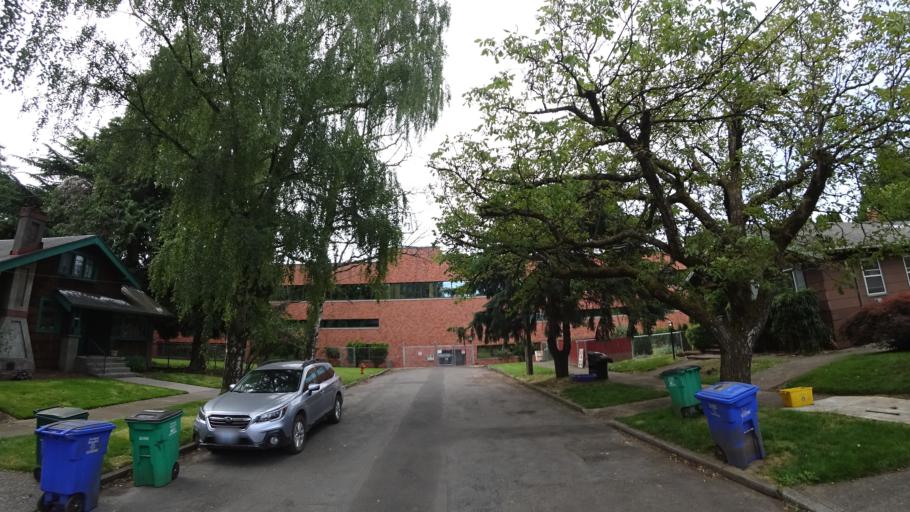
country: US
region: Oregon
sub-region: Multnomah County
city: Portland
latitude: 45.5328
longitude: -122.6162
